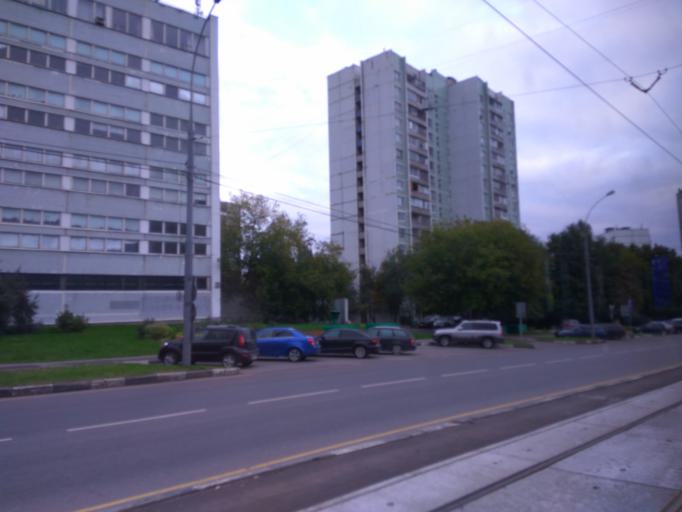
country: RU
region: Moscow
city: Chertanovo Yuzhnoye
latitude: 55.6002
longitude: 37.5888
